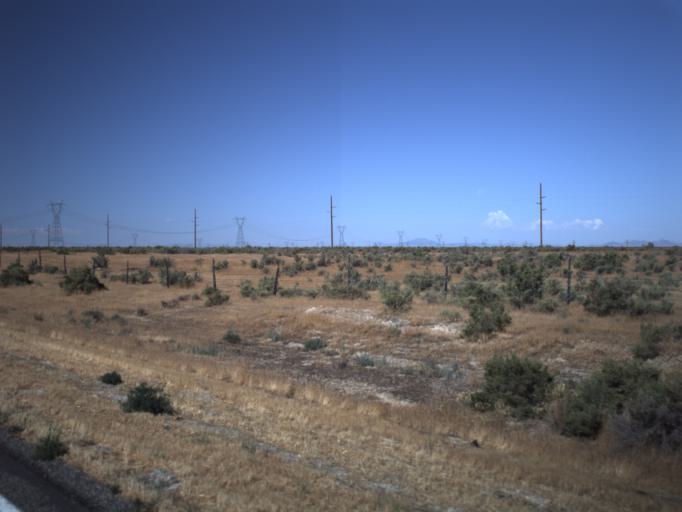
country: US
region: Utah
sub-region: Millard County
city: Delta
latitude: 39.4963
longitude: -112.3965
